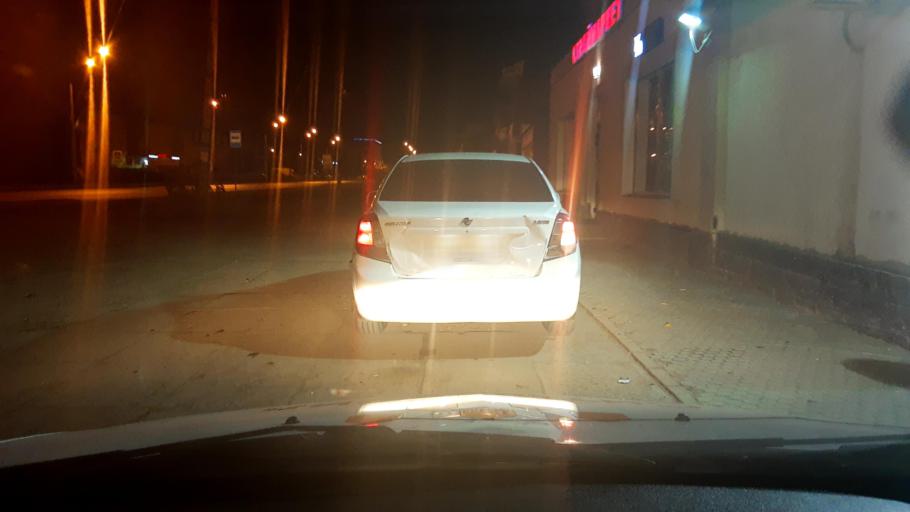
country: RU
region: Bashkortostan
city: Iglino
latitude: 54.7619
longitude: 56.2412
